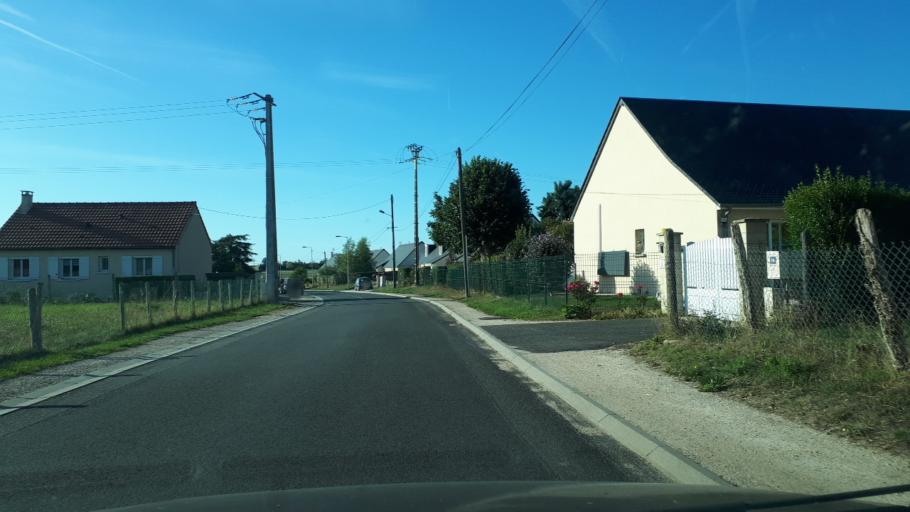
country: FR
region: Centre
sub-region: Departement d'Indre-et-Loire
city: Chateau-Renault
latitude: 47.6466
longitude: 0.9432
